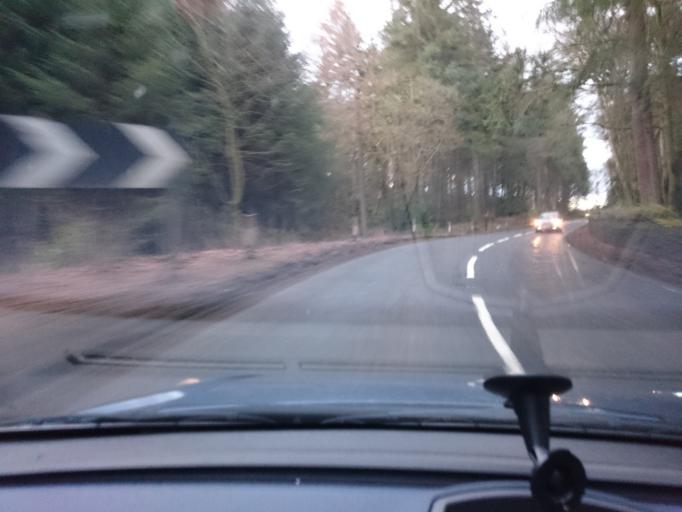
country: GB
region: Scotland
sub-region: Stirling
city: Doune
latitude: 56.2055
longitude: -4.1163
